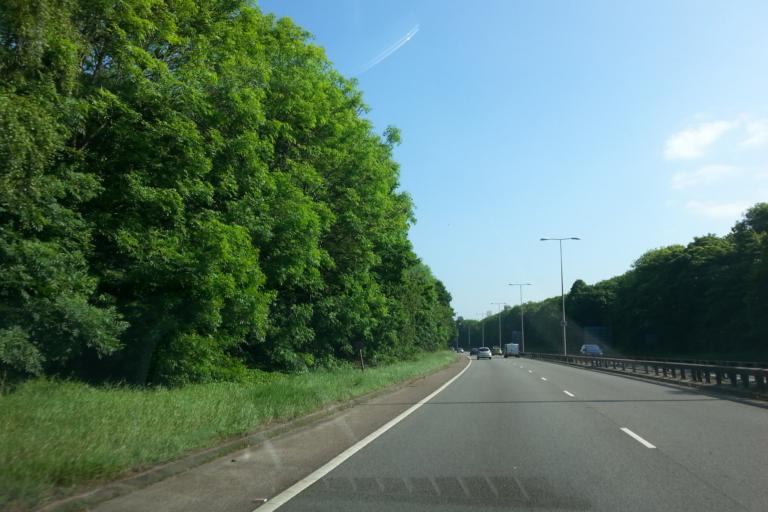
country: GB
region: England
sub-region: Peterborough
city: Marholm
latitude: 52.5787
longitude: -0.2840
